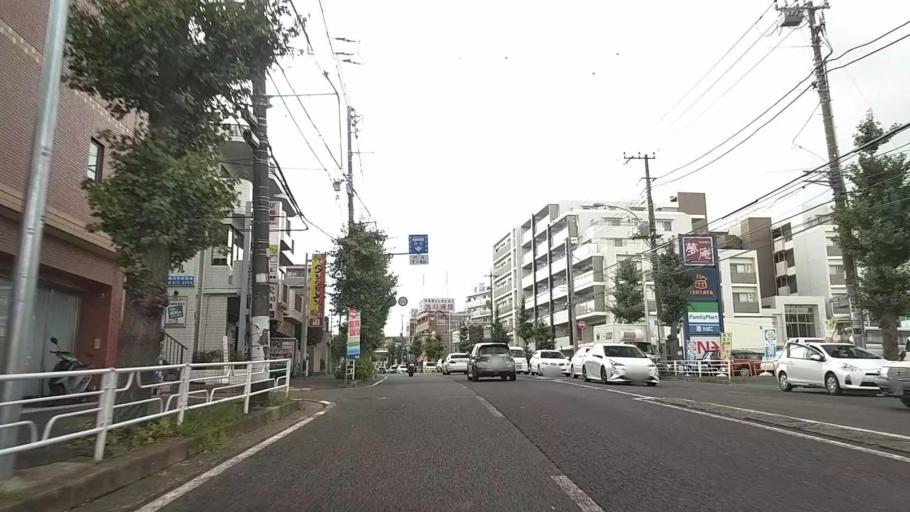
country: JP
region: Kanagawa
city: Yokohama
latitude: 35.4840
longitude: 139.6024
